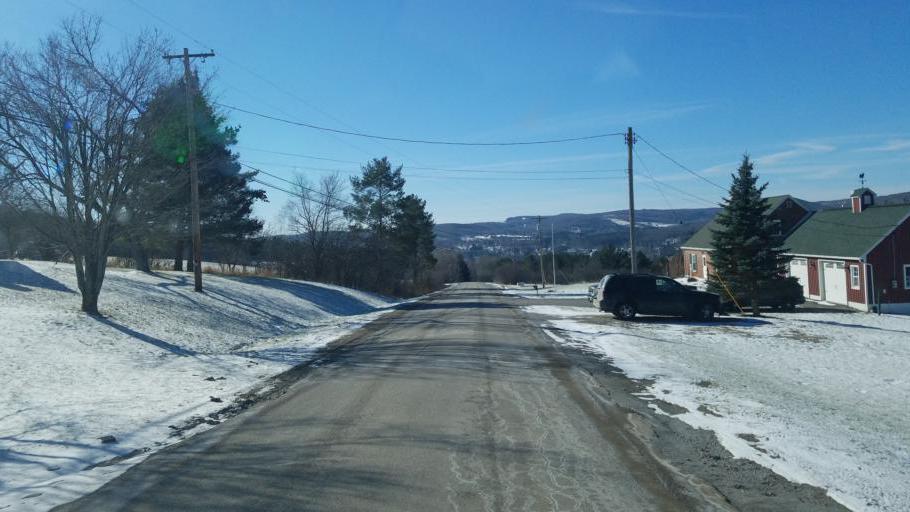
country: US
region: New York
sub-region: Allegany County
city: Wellsville
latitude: 42.1391
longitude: -77.9477
